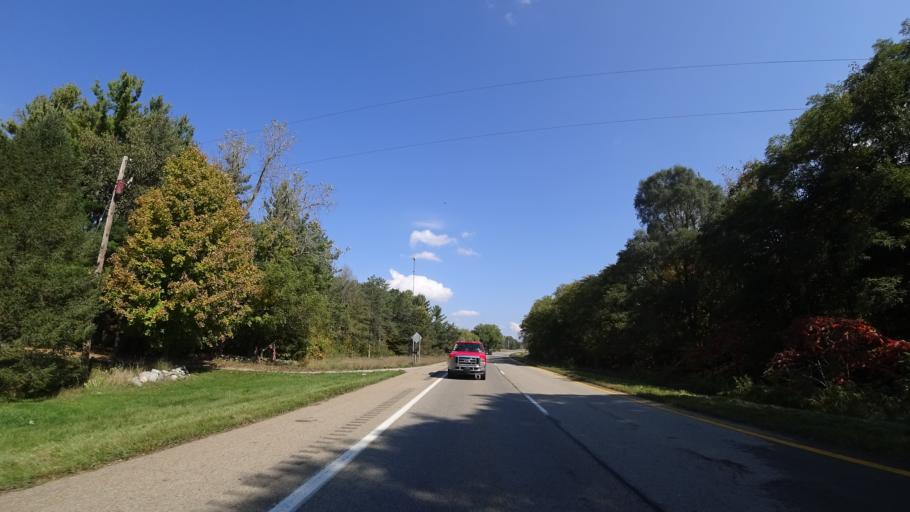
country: US
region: Michigan
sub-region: Calhoun County
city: Homer
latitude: 42.1598
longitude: -84.7689
